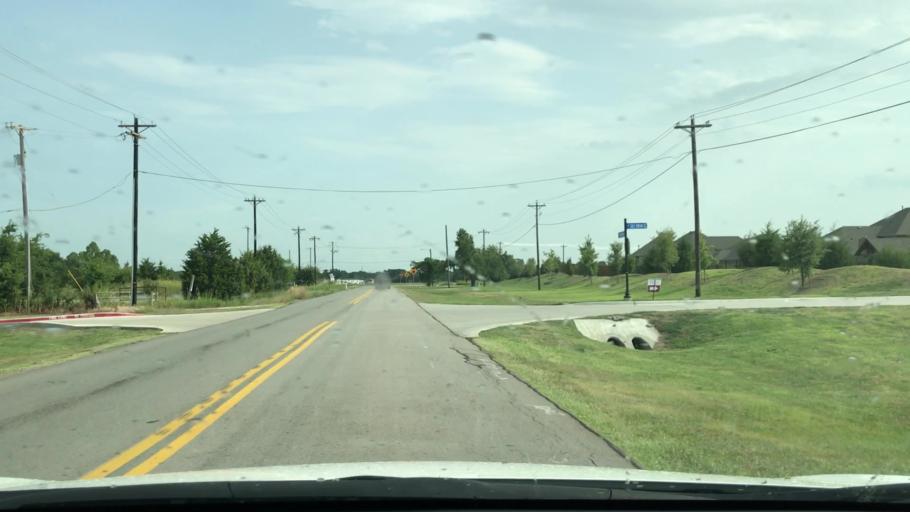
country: US
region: Texas
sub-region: Collin County
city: Wylie
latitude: 32.9850
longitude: -96.5218
